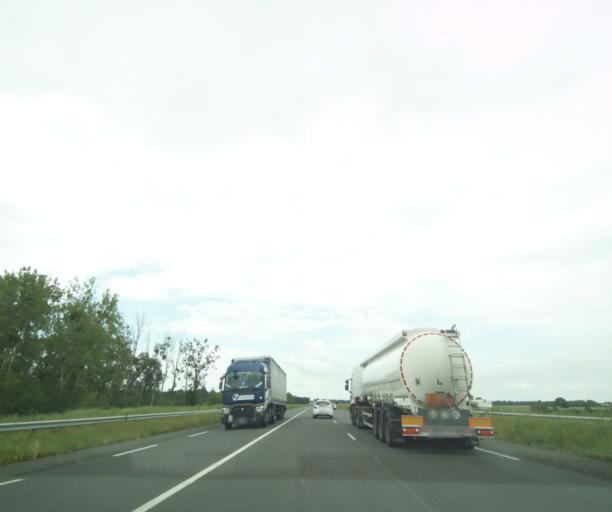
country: FR
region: Poitou-Charentes
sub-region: Departement des Deux-Sevres
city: Sainte-Verge
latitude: 47.0213
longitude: -0.2019
